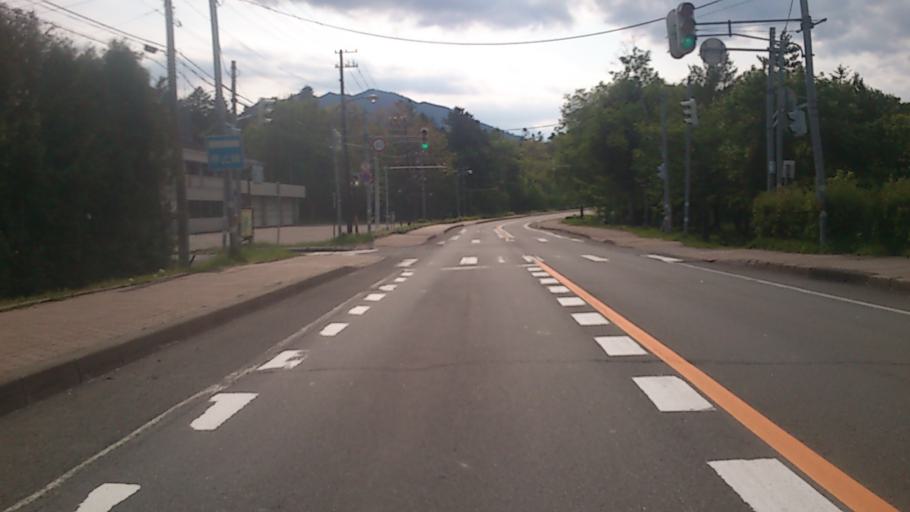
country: JP
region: Hokkaido
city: Bihoro
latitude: 43.4311
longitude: 144.0939
